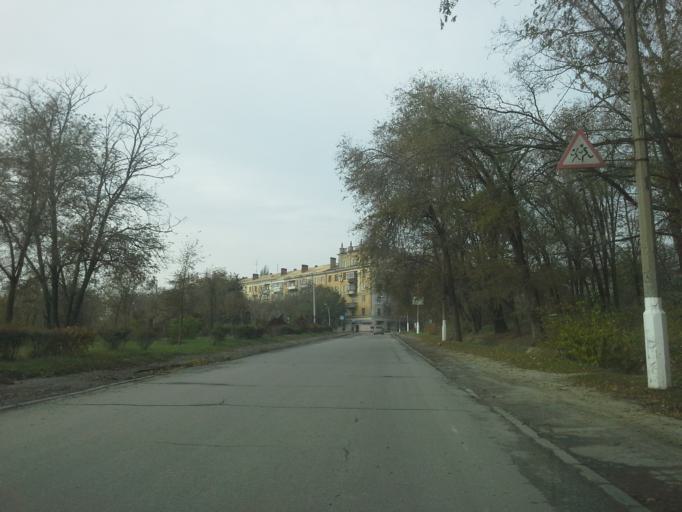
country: RU
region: Volgograd
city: Vodstroy
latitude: 48.7781
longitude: 44.5757
